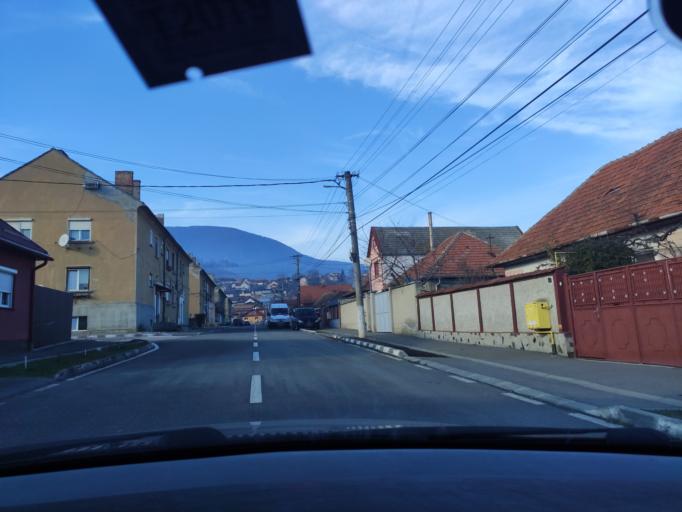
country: RO
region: Brasov
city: Codlea
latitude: 45.6910
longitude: 25.4419
